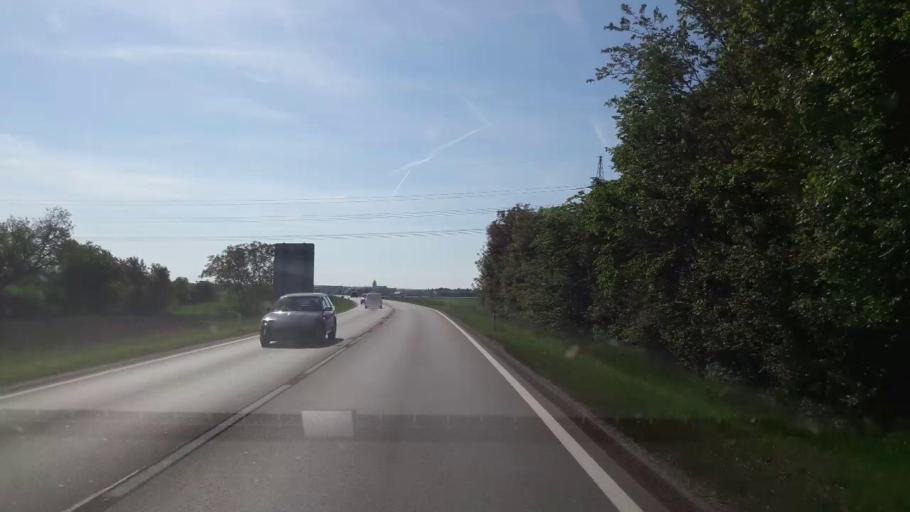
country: AT
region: Burgenland
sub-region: Eisenstadt-Umgebung
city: Trausdorf an der Wulka
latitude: 47.8215
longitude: 16.5379
